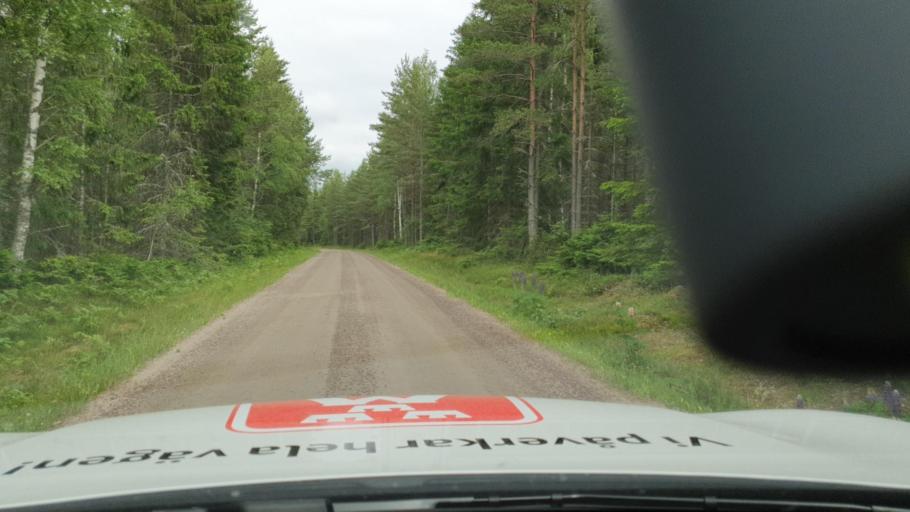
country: SE
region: Vaestra Goetaland
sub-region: Tidaholms Kommun
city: Tidaholm
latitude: 58.1644
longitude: 14.0447
